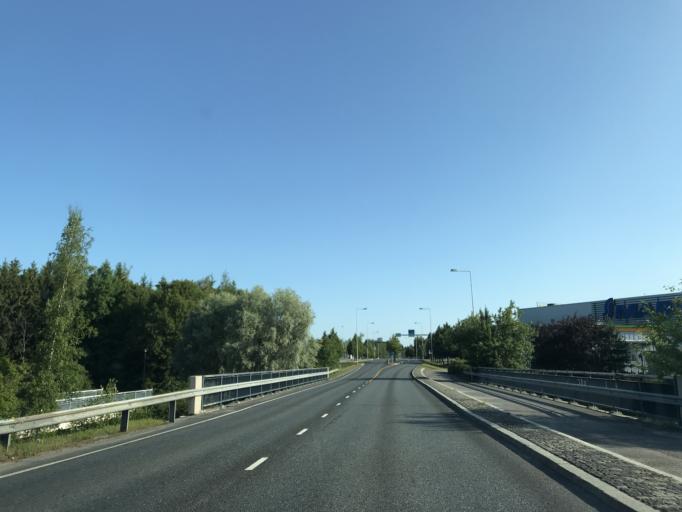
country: FI
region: Paijanne Tavastia
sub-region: Lahti
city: Orimattila
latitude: 60.8039
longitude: 25.7287
